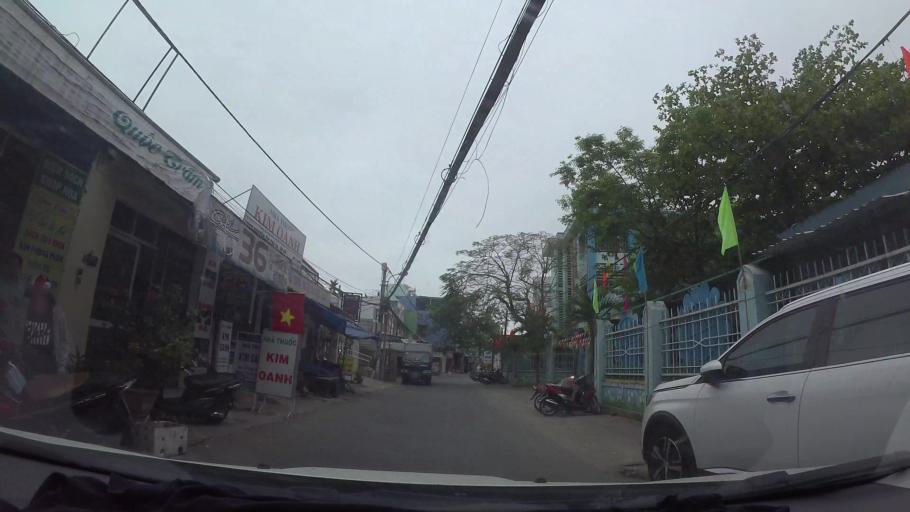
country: VN
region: Da Nang
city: Lien Chieu
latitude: 16.0718
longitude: 108.1475
